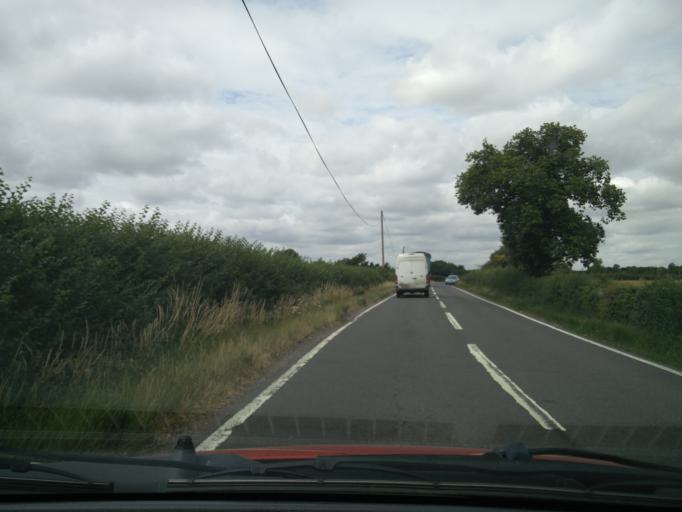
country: GB
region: England
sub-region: Essex
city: Burnham on Crouch
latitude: 51.6522
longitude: 0.7740
